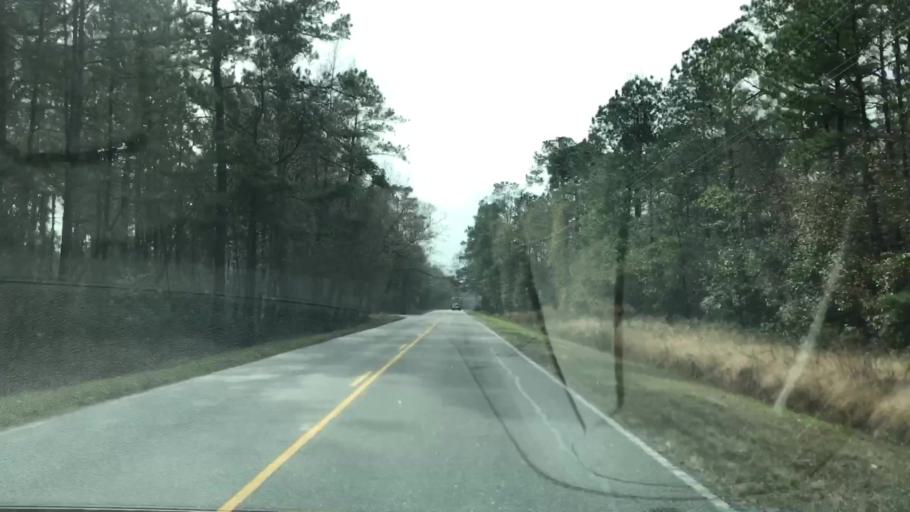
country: US
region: South Carolina
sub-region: Georgetown County
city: Murrells Inlet
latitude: 33.6436
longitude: -79.1756
